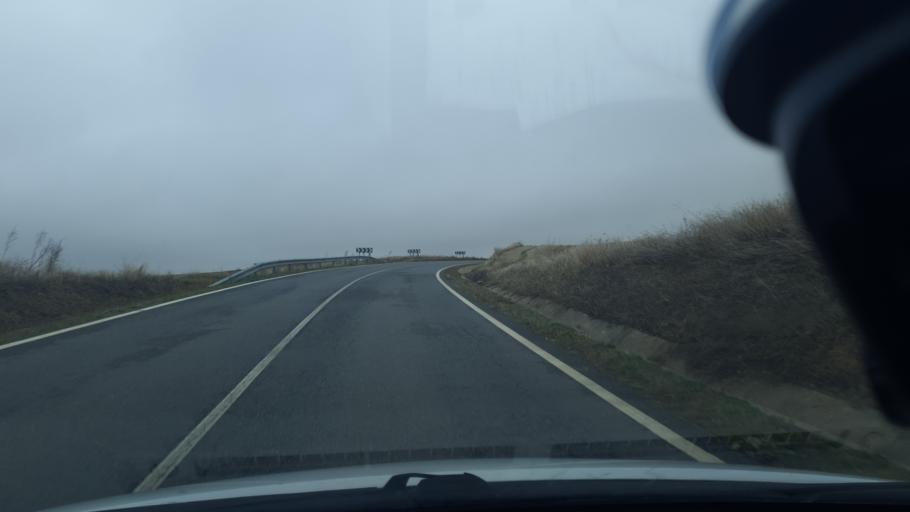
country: ES
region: Castille and Leon
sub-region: Provincia de Segovia
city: Valseca
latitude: 40.9959
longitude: -4.1828
